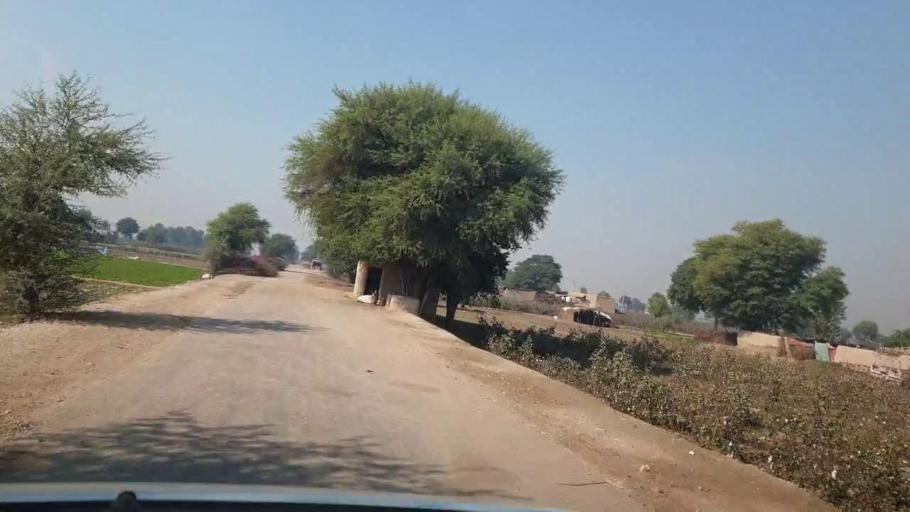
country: PK
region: Sindh
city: Bhan
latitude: 26.6116
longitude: 67.7683
